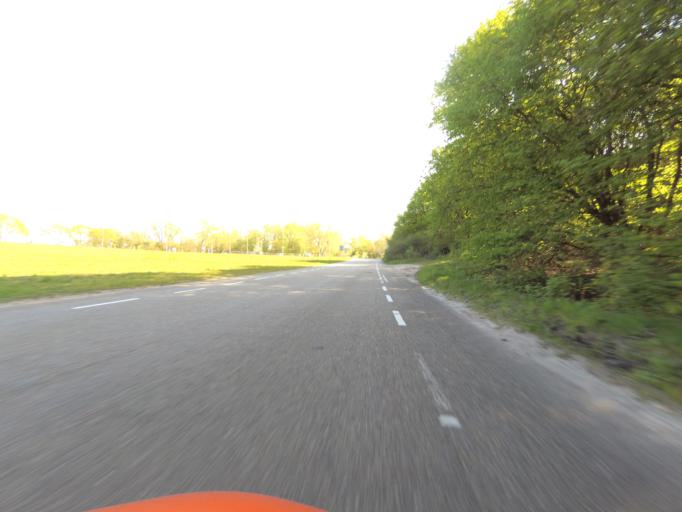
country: NL
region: North Holland
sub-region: Gemeente Naarden
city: Naarden
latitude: 52.3219
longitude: 5.1287
